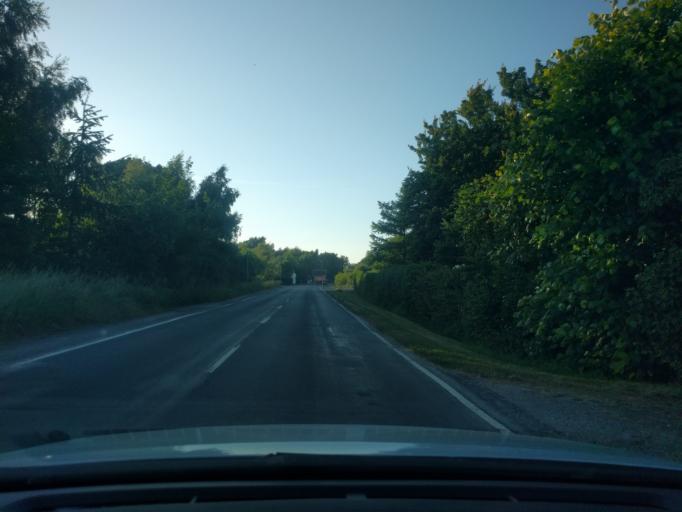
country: DK
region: South Denmark
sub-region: Kerteminde Kommune
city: Kerteminde
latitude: 55.5968
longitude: 10.6266
